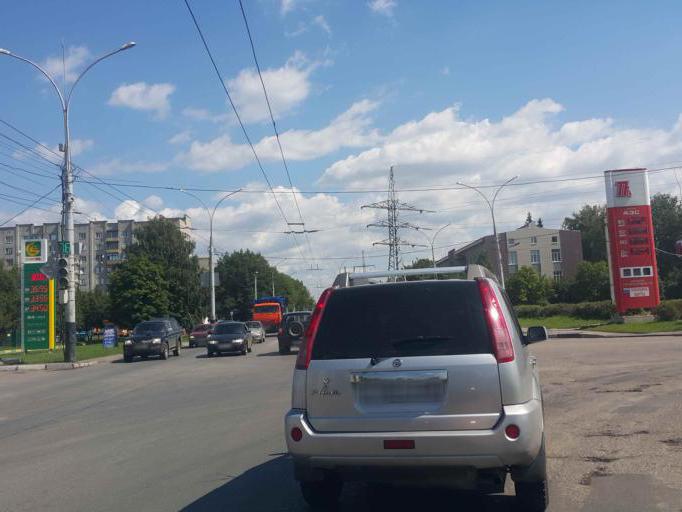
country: RU
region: Tambov
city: Tambov
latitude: 52.7482
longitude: 41.4591
